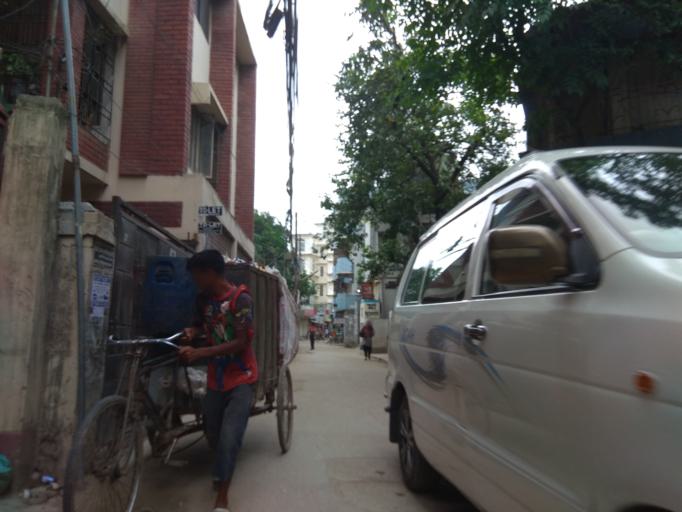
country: BD
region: Dhaka
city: Azimpur
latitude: 23.7959
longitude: 90.3781
